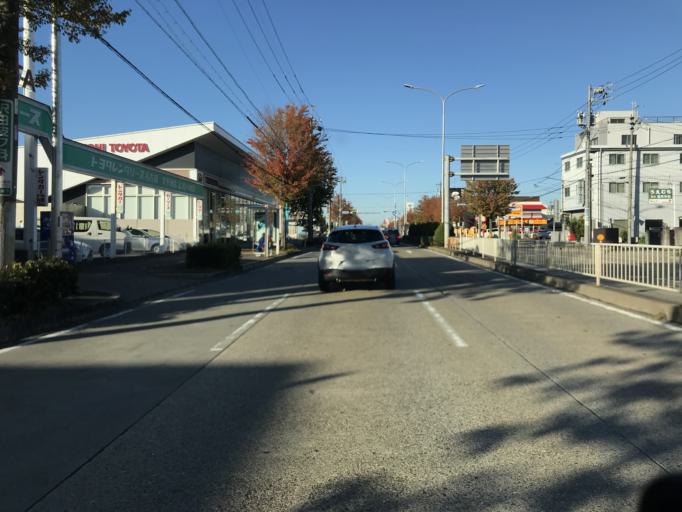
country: JP
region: Aichi
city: Nagoya-shi
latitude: 35.1256
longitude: 136.8691
